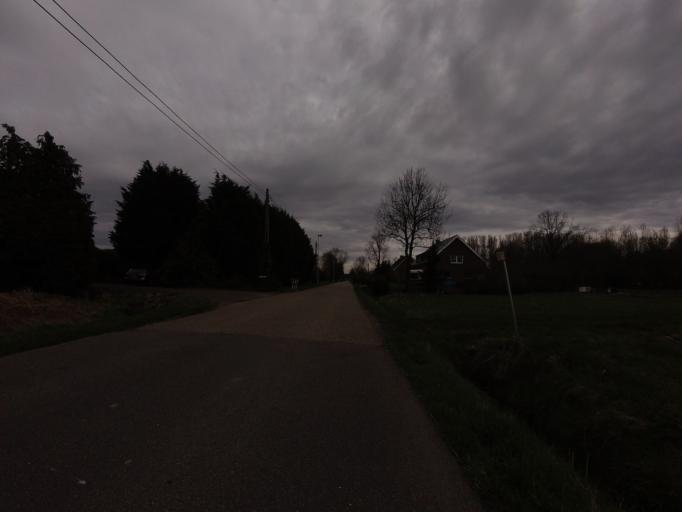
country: BE
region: Flanders
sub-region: Provincie Antwerpen
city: Lint
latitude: 51.1440
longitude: 4.5113
